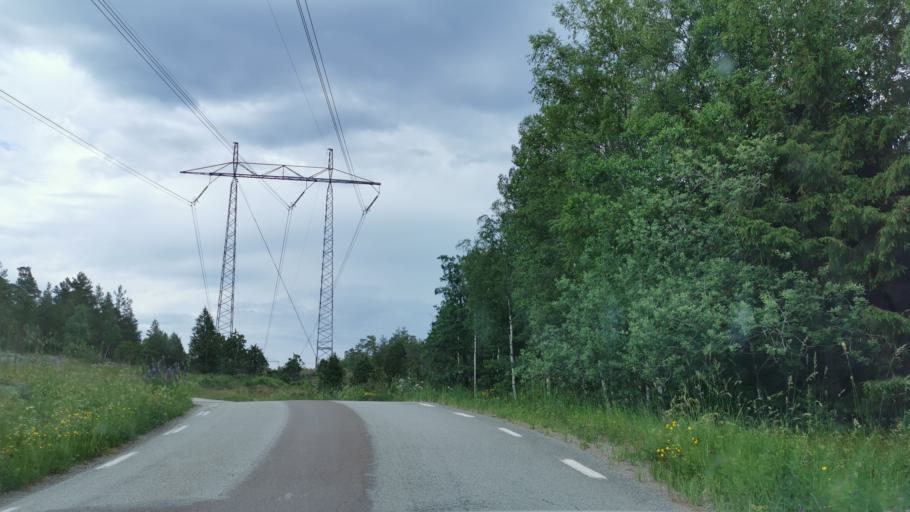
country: SE
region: Vaestra Goetaland
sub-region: Bengtsfors Kommun
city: Dals Langed
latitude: 58.8675
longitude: 12.4031
